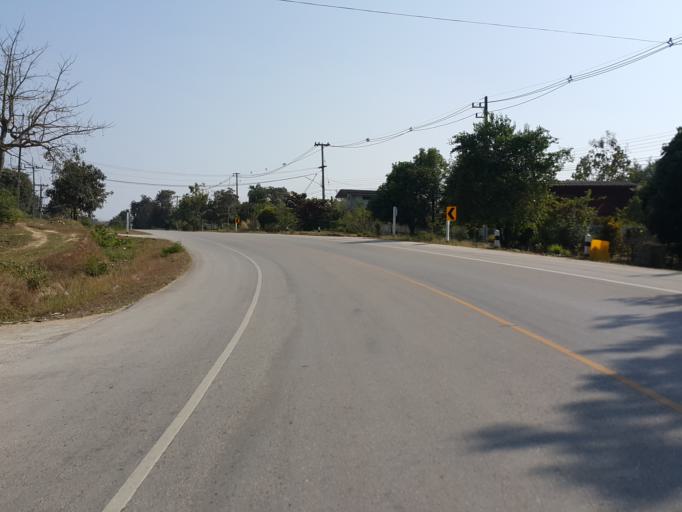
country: TH
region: Lampang
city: Chae Hom
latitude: 18.7364
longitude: 99.5778
